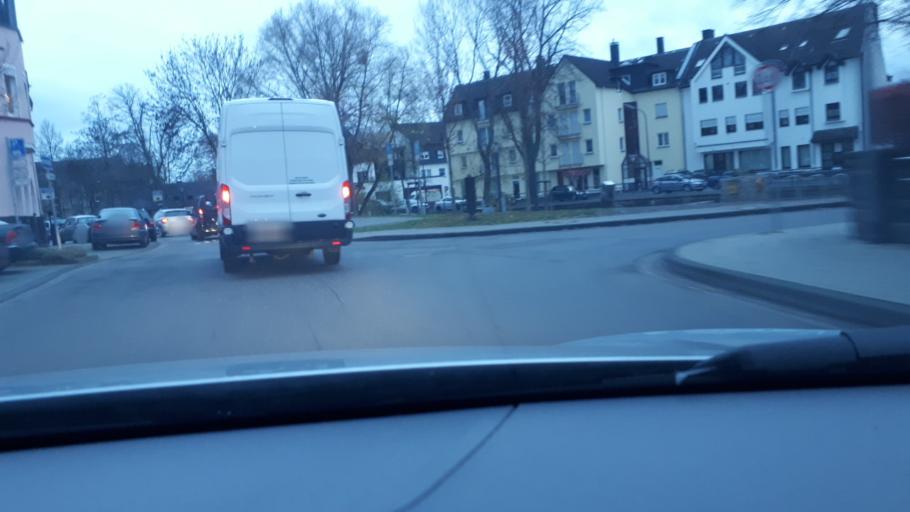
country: DE
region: Rheinland-Pfalz
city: Mayen
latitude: 50.3293
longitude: 7.2260
